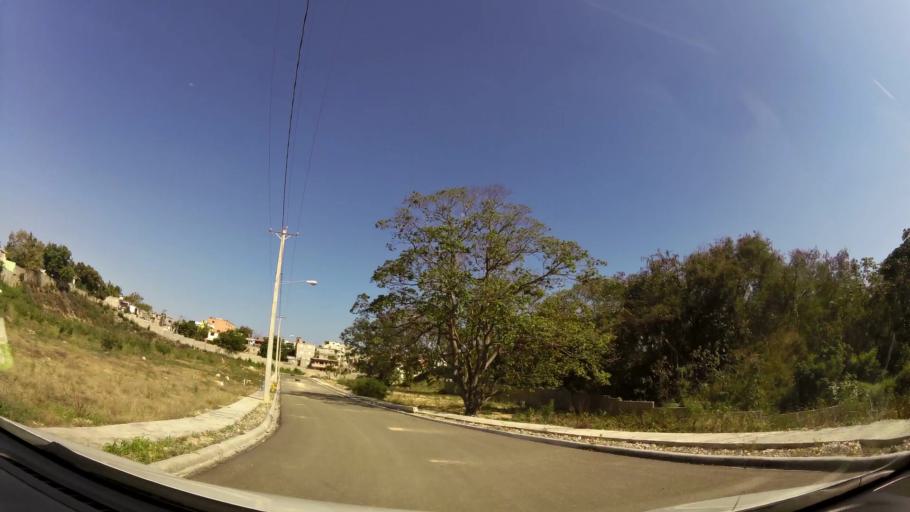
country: DO
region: Nacional
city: Bella Vista
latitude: 18.4573
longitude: -69.9810
